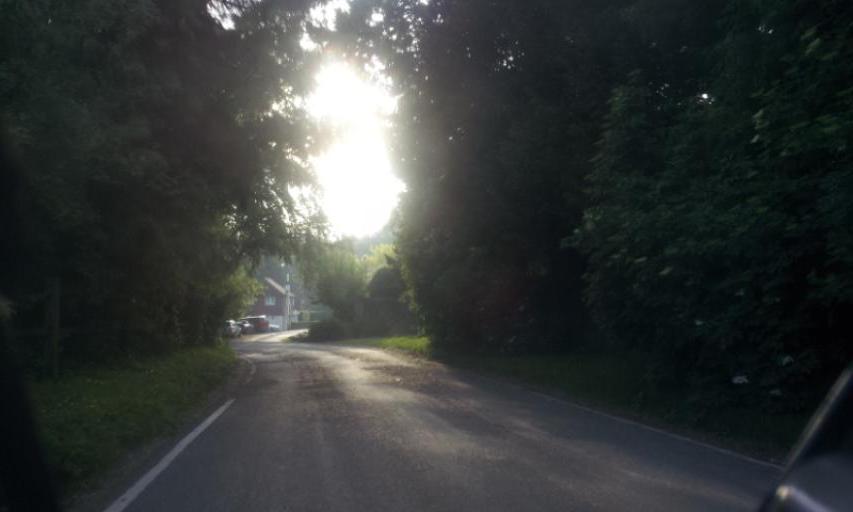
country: GB
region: England
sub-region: Kent
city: Harrietsham
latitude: 51.2455
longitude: 0.6827
